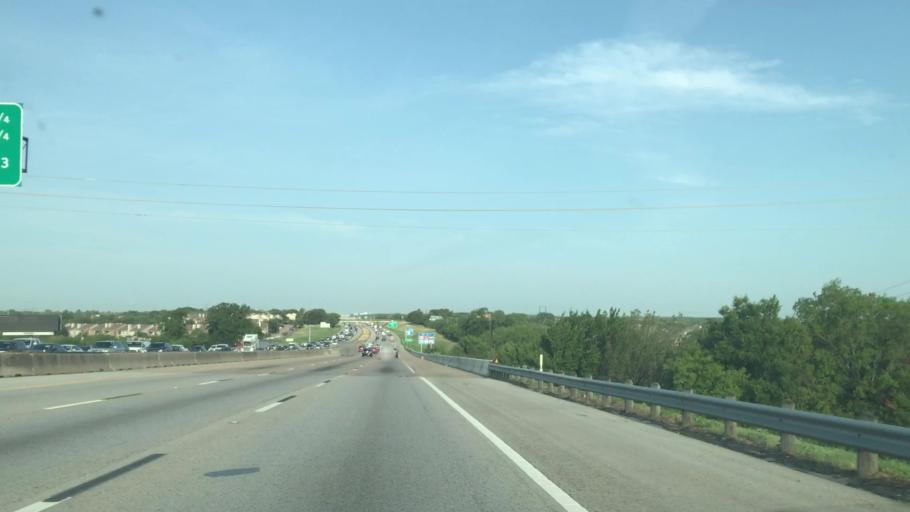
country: US
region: Texas
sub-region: Tarrant County
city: Pantego
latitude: 32.7602
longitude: -97.1481
